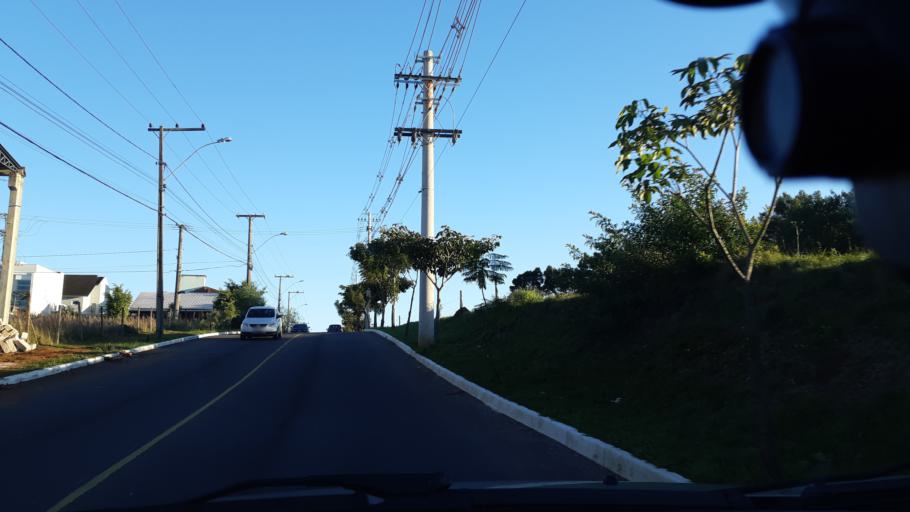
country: BR
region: Rio Grande do Sul
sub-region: Canoas
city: Canoas
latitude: -29.9138
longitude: -51.1541
